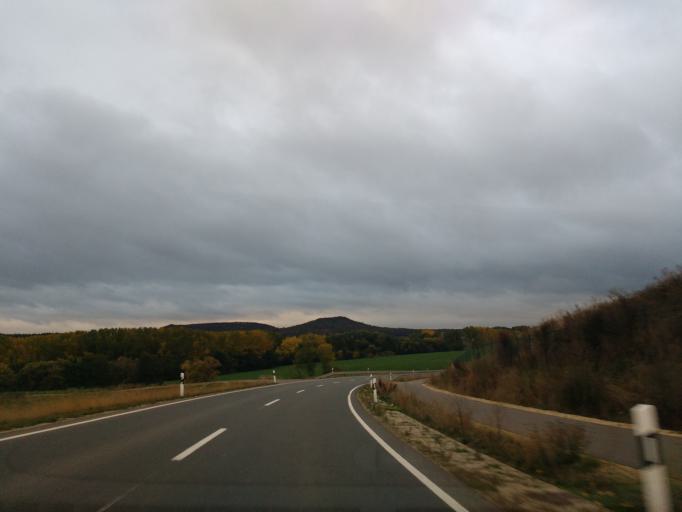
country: DE
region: Thuringia
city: Grossbodungen
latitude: 51.4648
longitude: 10.4643
